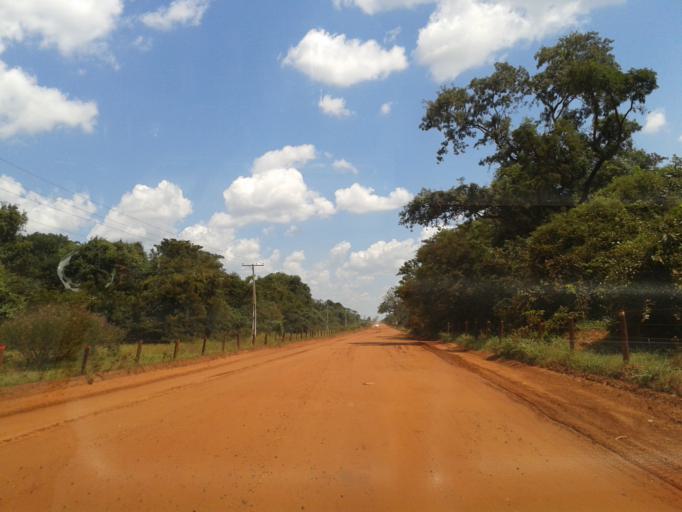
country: BR
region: Minas Gerais
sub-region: Ituiutaba
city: Ituiutaba
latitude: -19.0007
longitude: -49.6672
